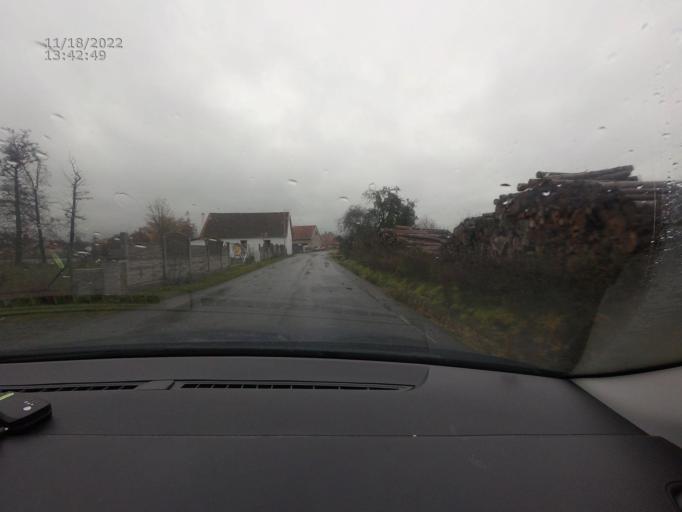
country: CZ
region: Plzensky
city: Kasejovice
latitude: 49.4351
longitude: 13.8051
